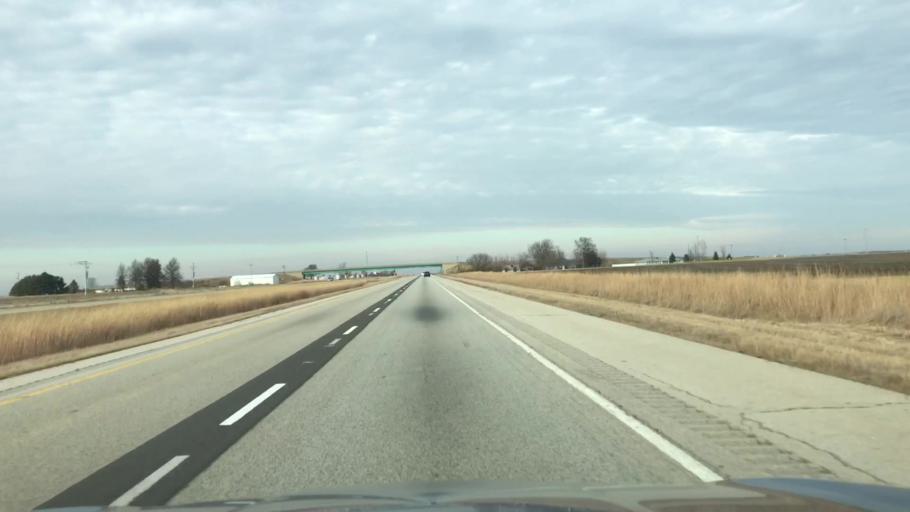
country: US
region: Illinois
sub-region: Sangamon County
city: Divernon
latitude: 39.5192
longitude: -89.6453
